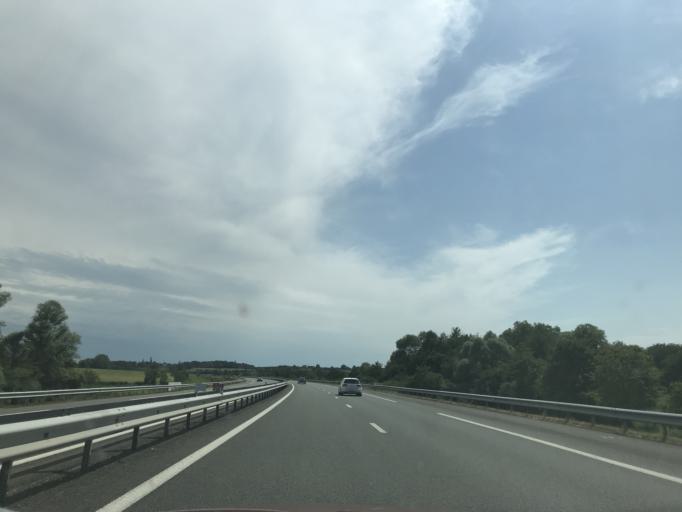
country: FR
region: Centre
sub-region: Departement du Cher
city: Orval
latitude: 46.6894
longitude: 2.4594
